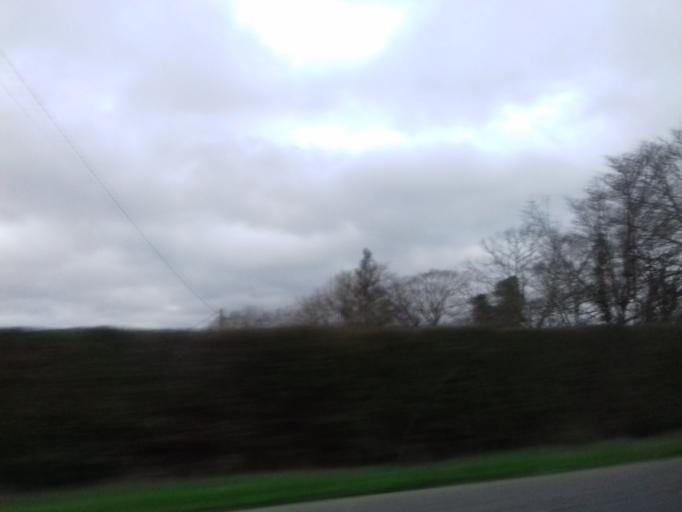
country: IE
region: Munster
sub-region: County Limerick
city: Abbeyfeale
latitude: 52.3882
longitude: -9.2781
